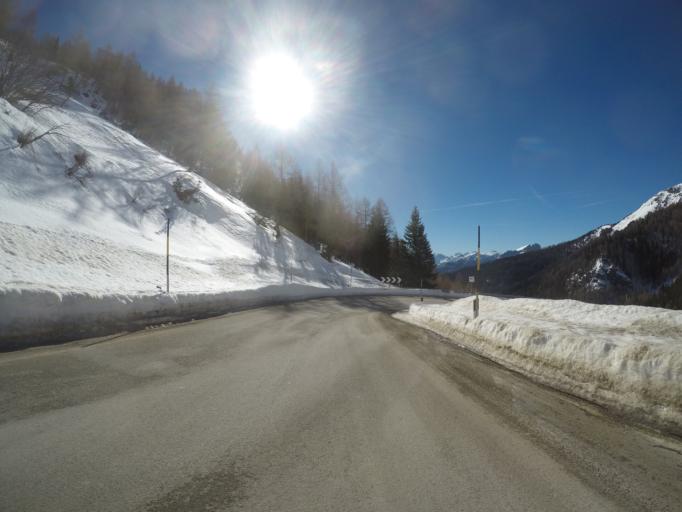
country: IT
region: Veneto
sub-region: Provincia di Belluno
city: Selva di Cadore
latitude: 46.4807
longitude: 12.0344
